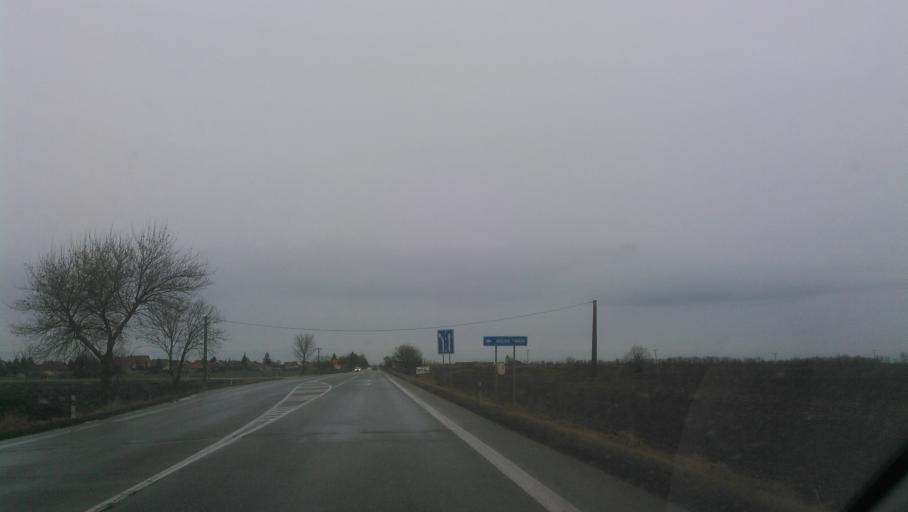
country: SK
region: Nitriansky
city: Sellye
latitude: 48.1718
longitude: 17.8297
